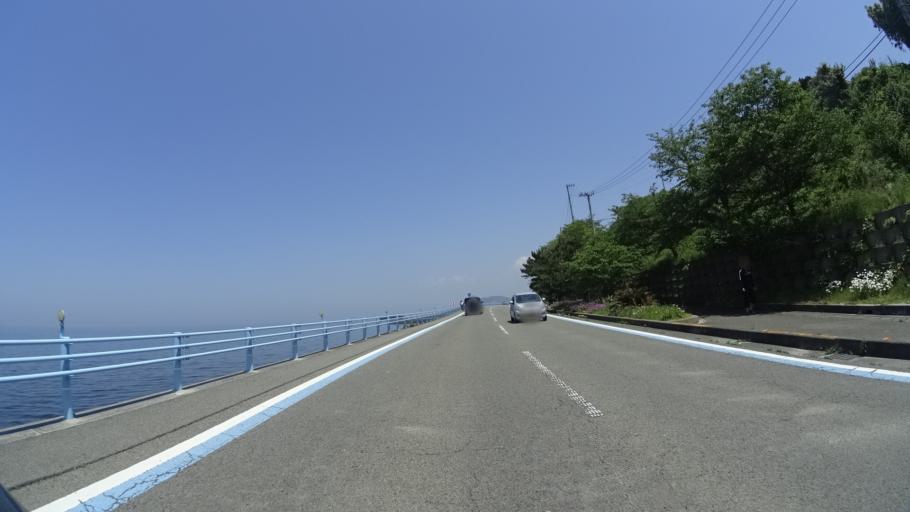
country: JP
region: Ehime
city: Iyo
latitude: 33.6828
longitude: 132.6296
